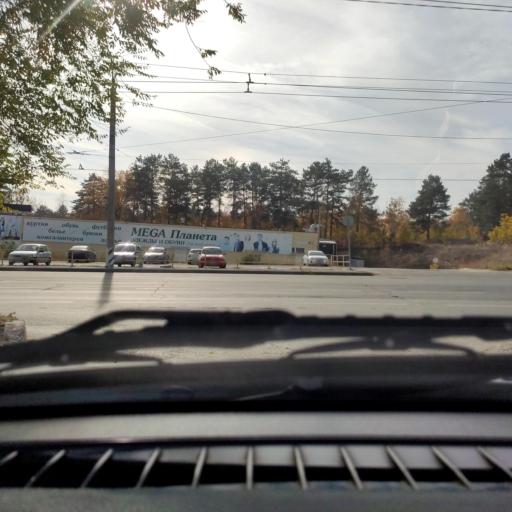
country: RU
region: Samara
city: Zhigulevsk
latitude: 53.4762
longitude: 49.4589
